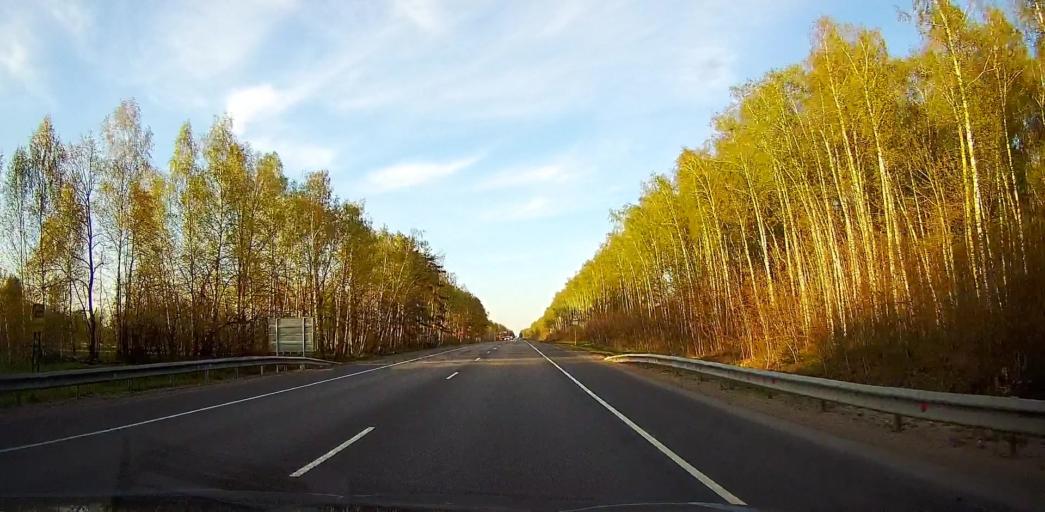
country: RU
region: Moskovskaya
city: Meshcherino
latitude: 55.2377
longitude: 38.4242
